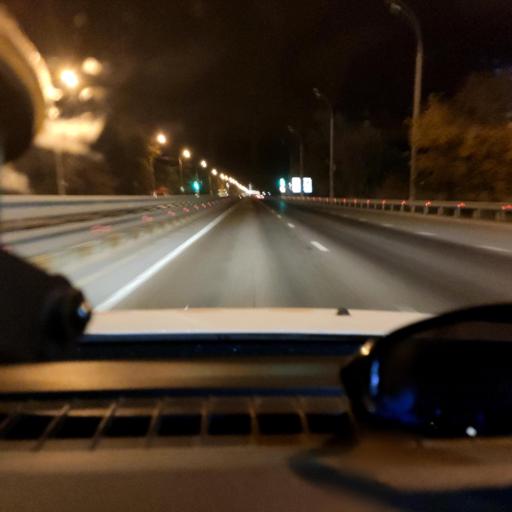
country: RU
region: Samara
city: Samara
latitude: 53.1130
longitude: 50.1657
